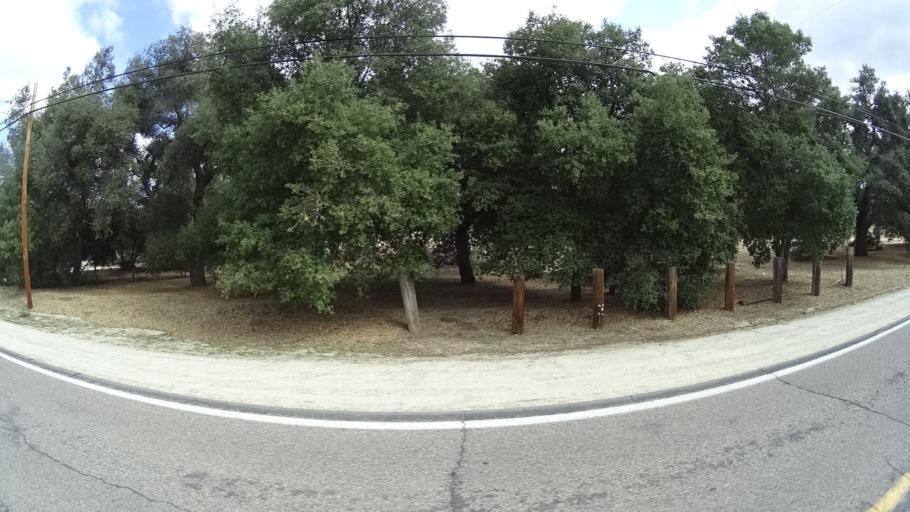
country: US
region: California
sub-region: San Diego County
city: Campo
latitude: 32.6691
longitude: -116.4884
